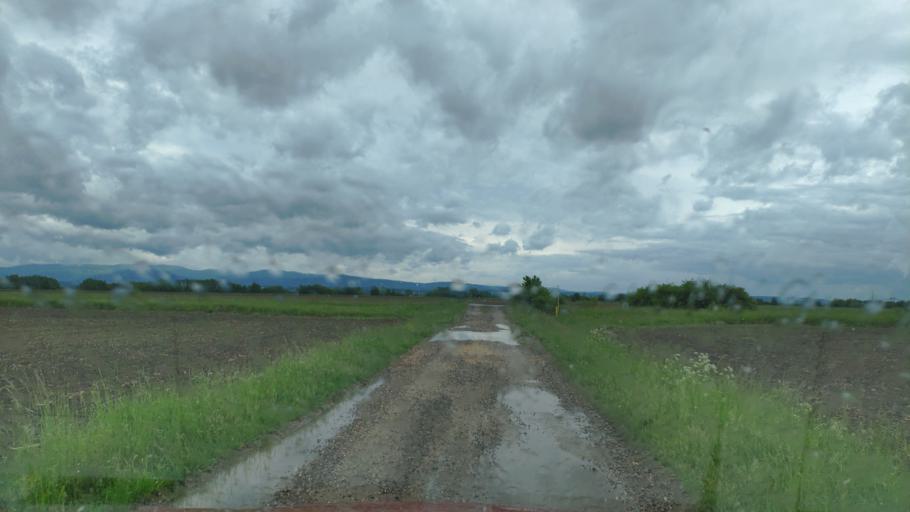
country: SK
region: Kosicky
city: Moldava nad Bodvou
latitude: 48.5507
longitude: 21.1136
